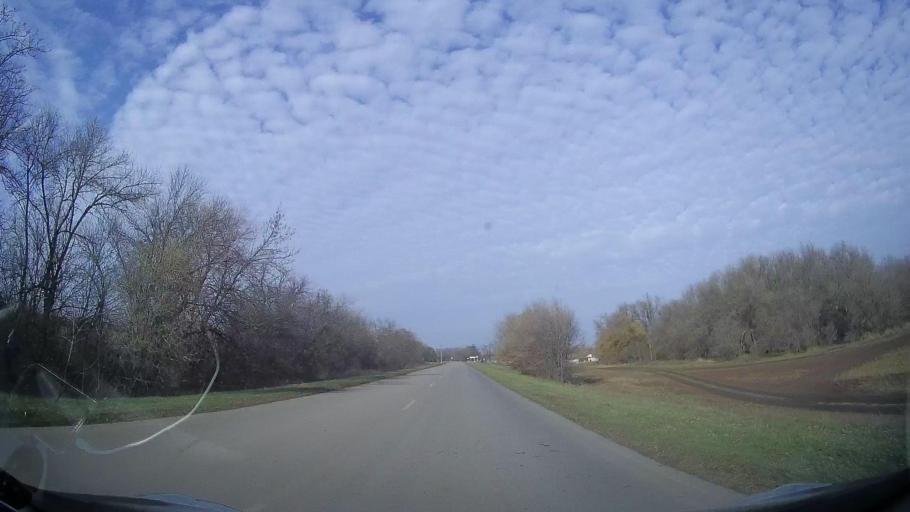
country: RU
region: Rostov
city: Gigant
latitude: 46.8328
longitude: 41.3352
